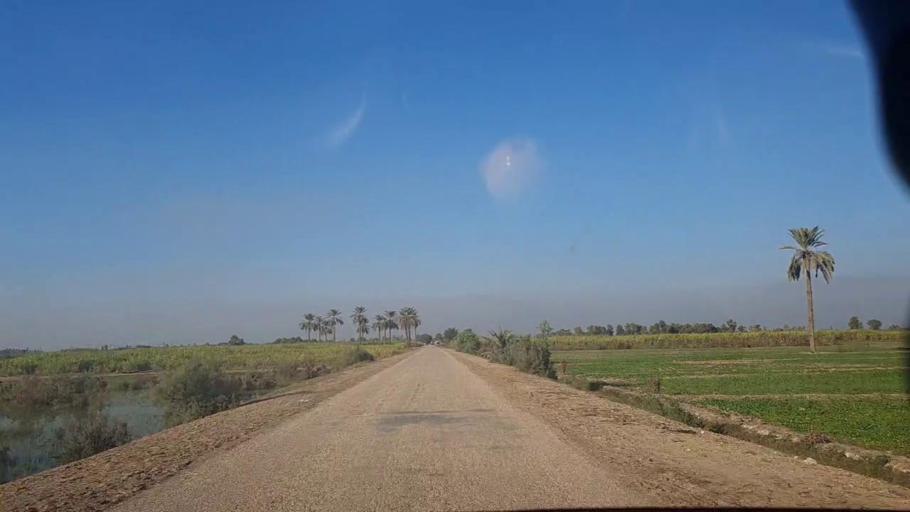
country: PK
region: Sindh
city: Sobhadero
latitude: 27.4089
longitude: 68.4223
